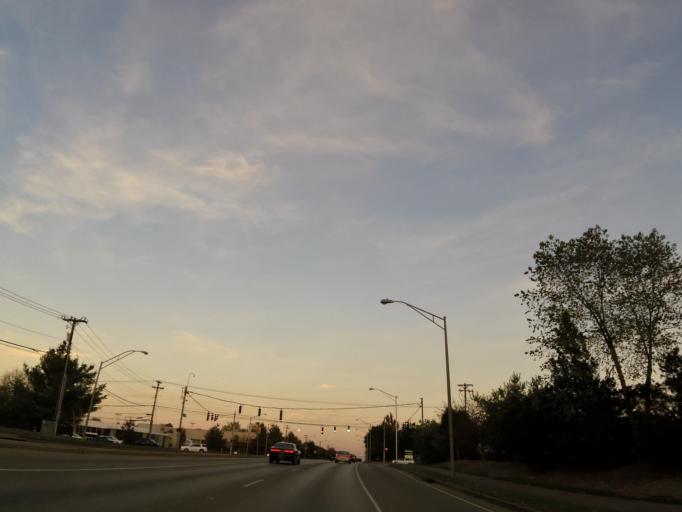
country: US
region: Kentucky
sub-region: Fayette County
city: Lexington
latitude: 38.0066
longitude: -84.4372
